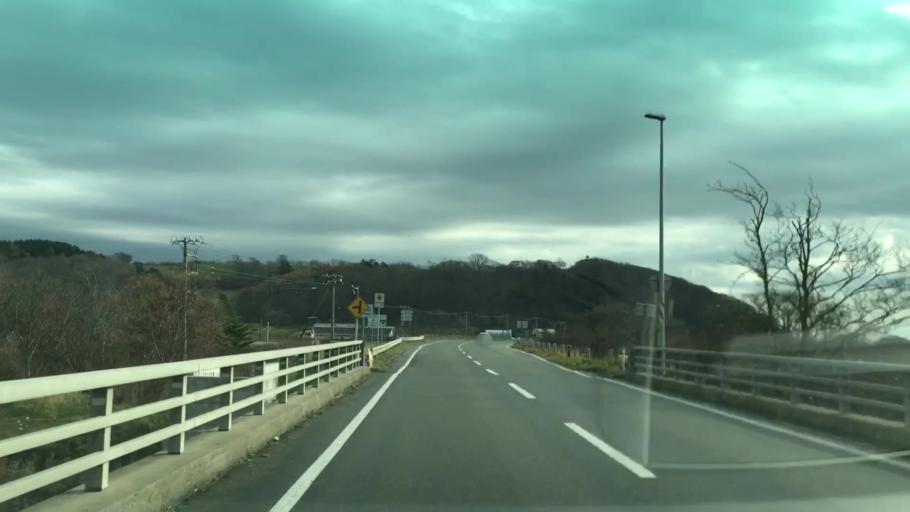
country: JP
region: Hokkaido
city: Shizunai-furukawacho
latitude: 42.1424
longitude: 142.8494
